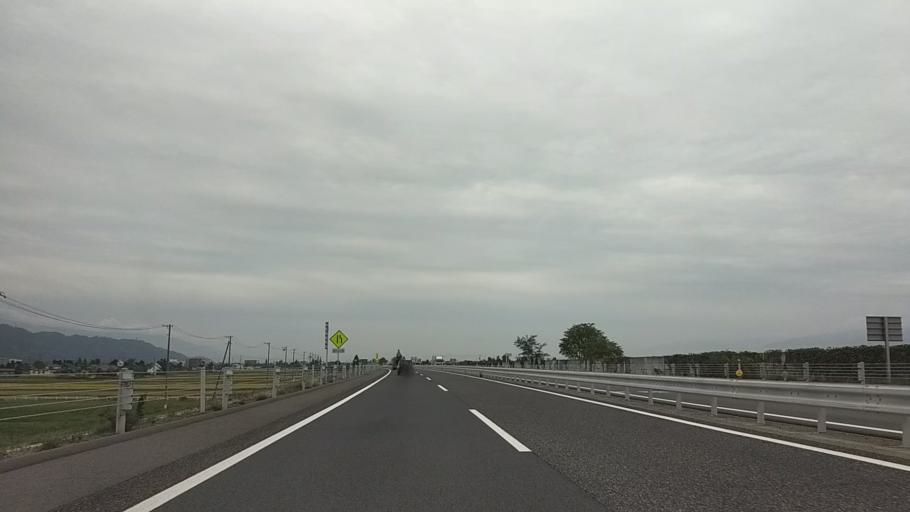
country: JP
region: Nagano
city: Toyoshina
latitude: 36.3124
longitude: 137.9206
